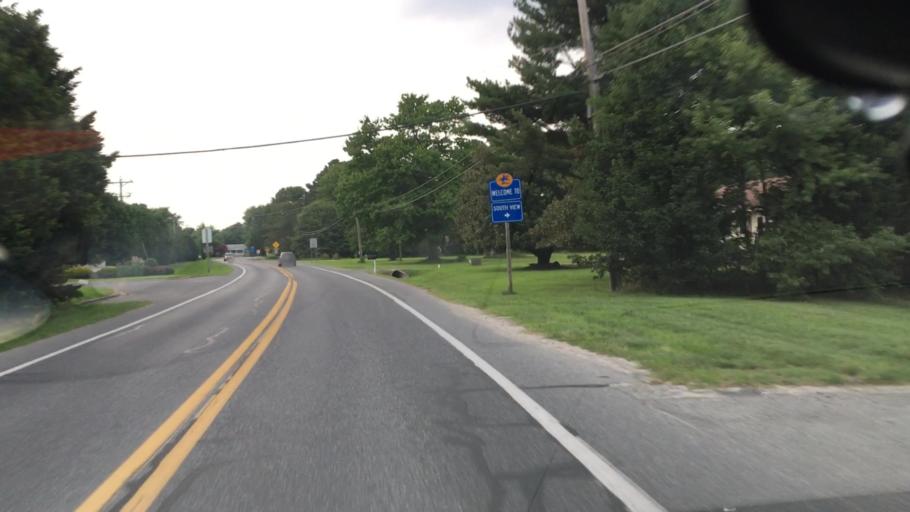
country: US
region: Delaware
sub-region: Sussex County
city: Ocean View
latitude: 38.5351
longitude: -75.0896
